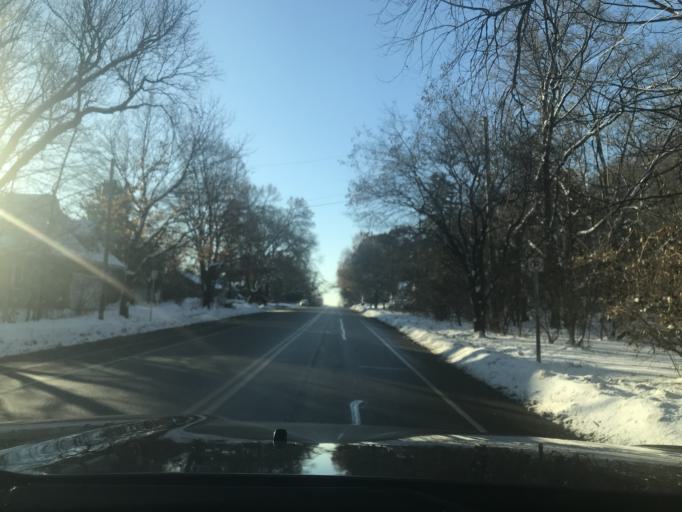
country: US
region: Minnesota
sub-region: Dakota County
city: Mendota Heights
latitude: 44.9241
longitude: -93.1467
